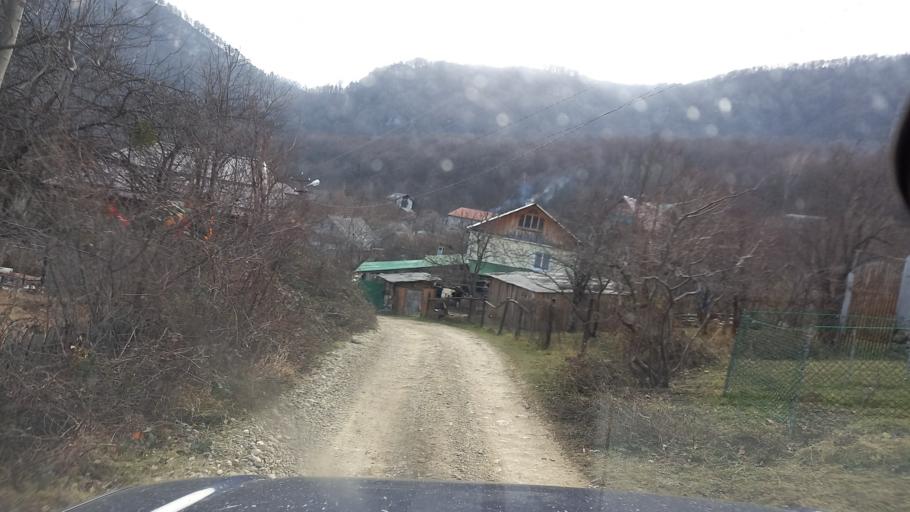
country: RU
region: Krasnodarskiy
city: Neftegorsk
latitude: 44.2292
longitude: 39.8994
